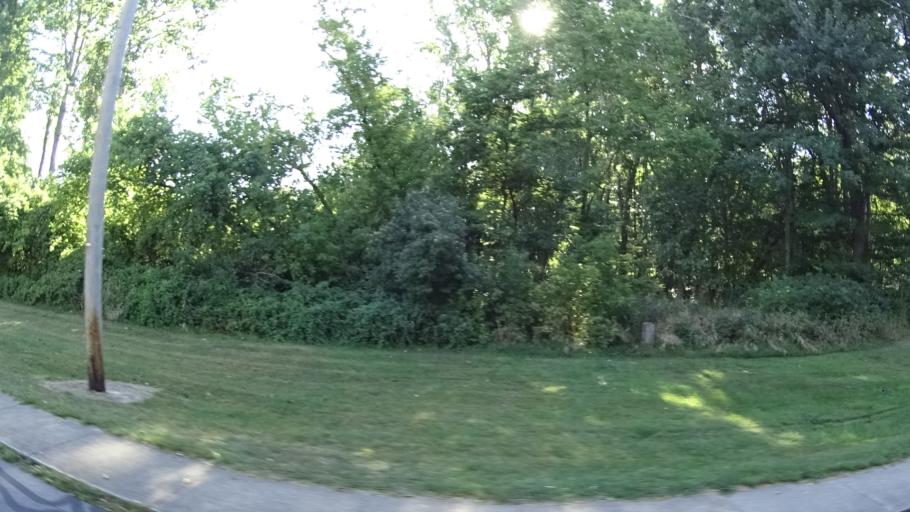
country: US
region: Ohio
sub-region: Erie County
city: Sandusky
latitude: 41.6110
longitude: -82.7077
